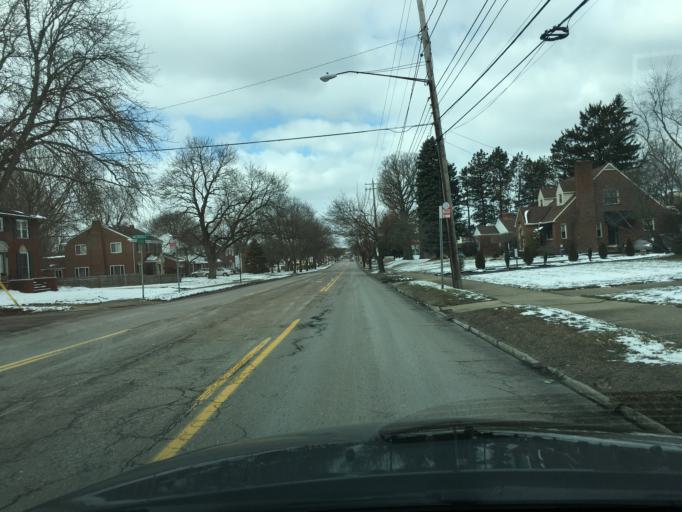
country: US
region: Ohio
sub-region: Summit County
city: Fairlawn
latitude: 41.1058
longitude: -81.5646
